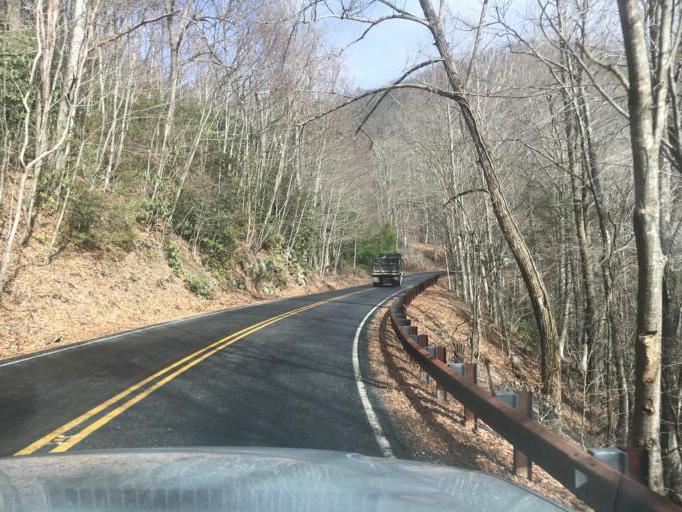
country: US
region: North Carolina
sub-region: Haywood County
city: Canton
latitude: 35.3745
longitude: -82.8147
